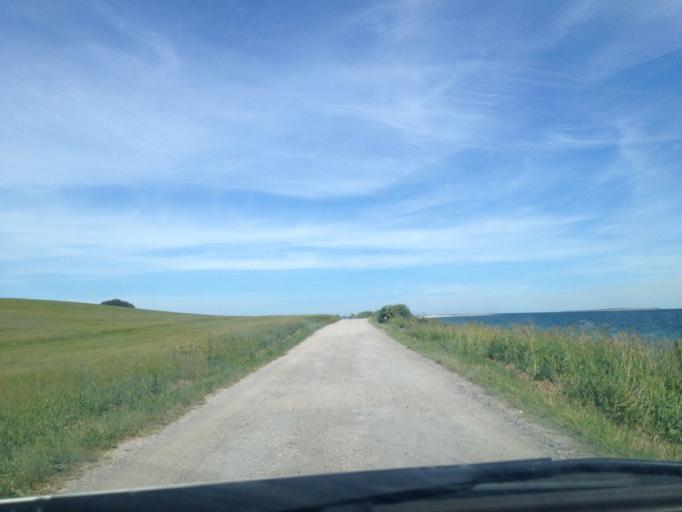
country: DK
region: Central Jutland
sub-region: Samso Kommune
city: Tranebjerg
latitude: 55.8801
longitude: 10.6769
